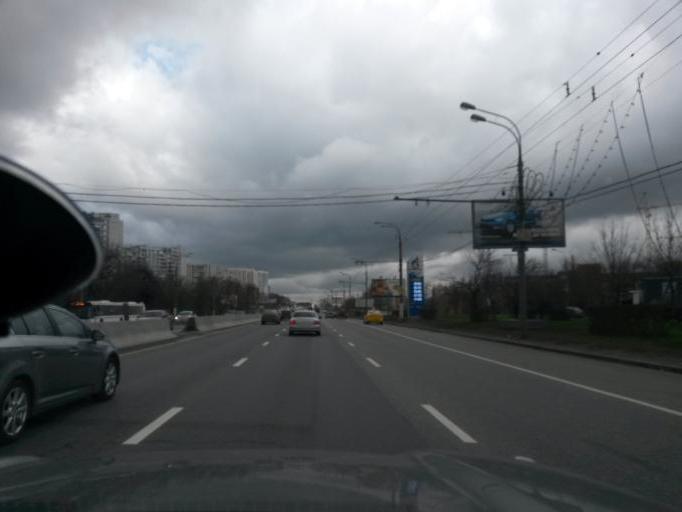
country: RU
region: Moscow
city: Annino
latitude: 55.5848
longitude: 37.5980
